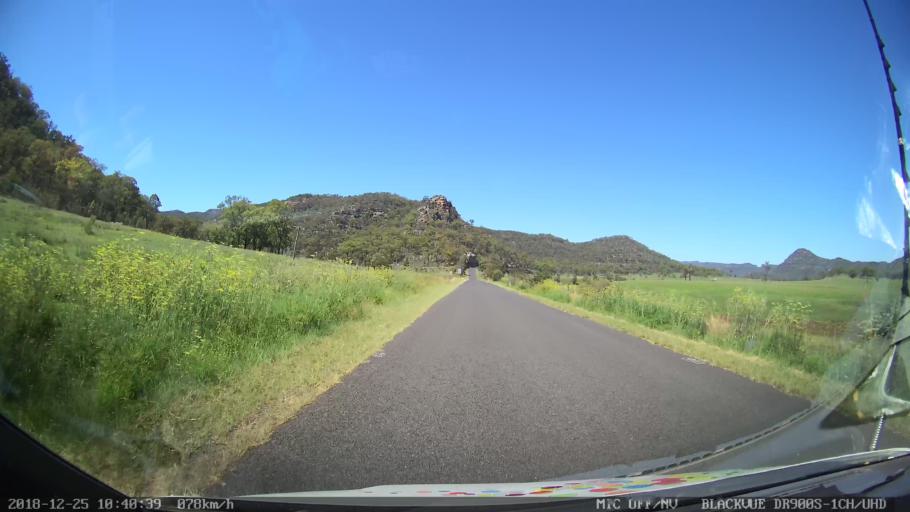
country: AU
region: New South Wales
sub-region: Upper Hunter Shire
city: Merriwa
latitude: -32.4098
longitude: 150.3416
